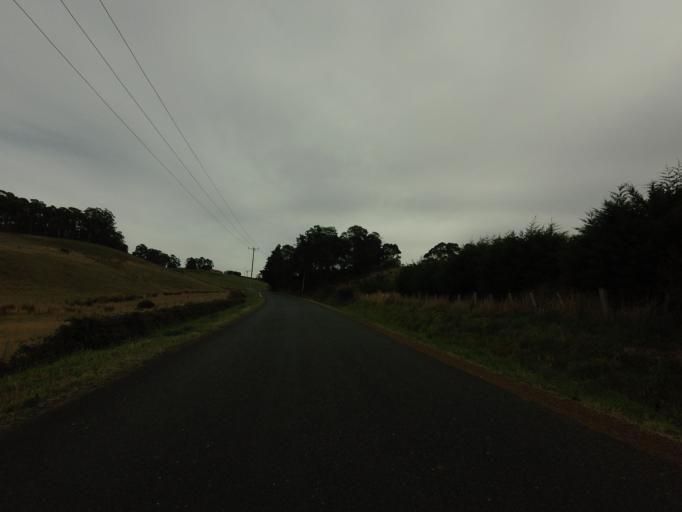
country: AU
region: Tasmania
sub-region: Sorell
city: Sorell
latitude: -42.5348
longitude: 147.5677
